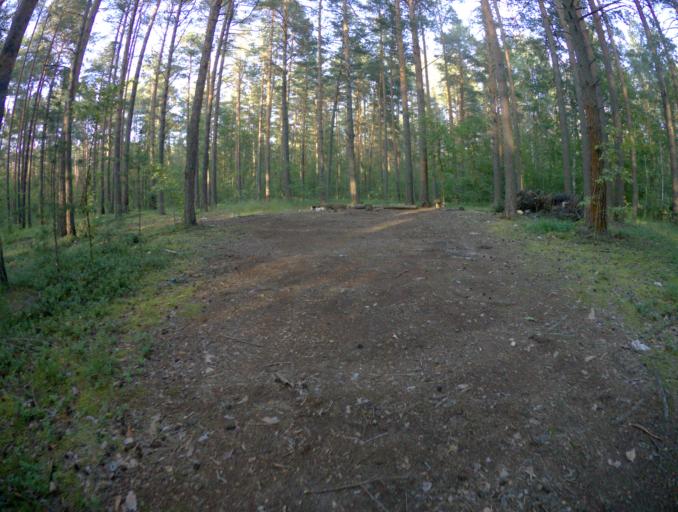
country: RU
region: Vladimir
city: Kommunar
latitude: 56.0944
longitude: 40.4519
